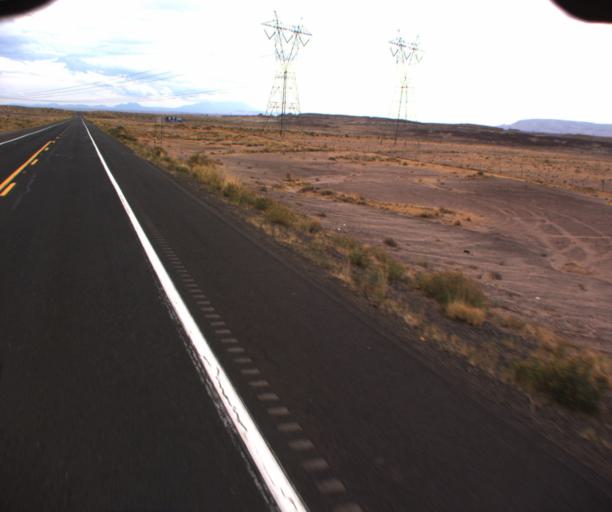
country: US
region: Arizona
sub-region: Coconino County
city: Tuba City
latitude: 35.9811
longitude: -111.3944
